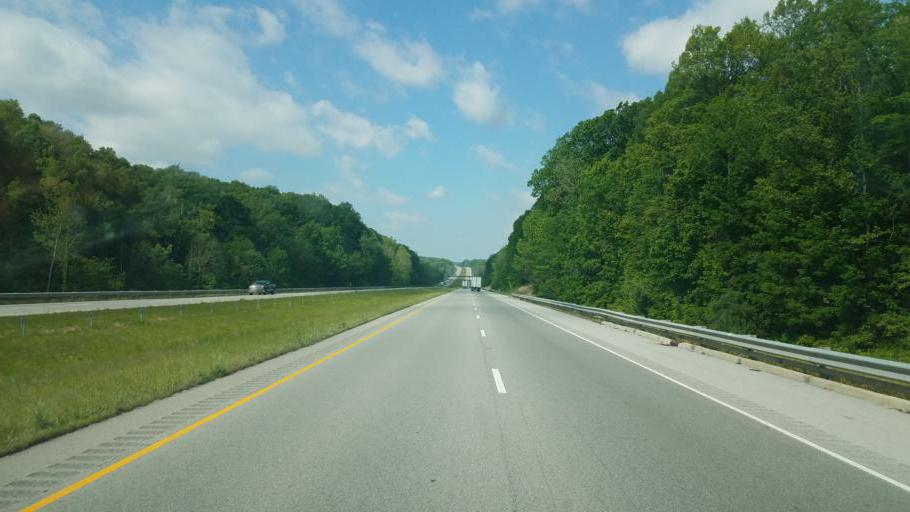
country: US
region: Indiana
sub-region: Clay County
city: Brazil
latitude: 39.4953
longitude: -86.9817
